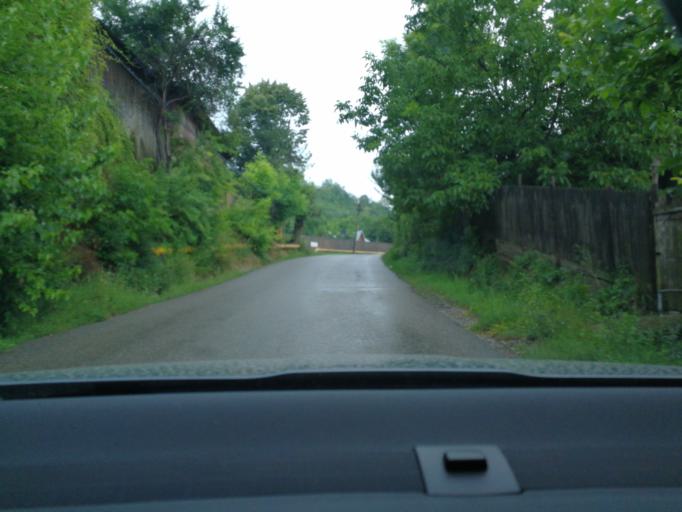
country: RO
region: Prahova
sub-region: Comuna Ceptura
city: Ceptura de Jos
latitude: 45.0356
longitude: 26.3174
